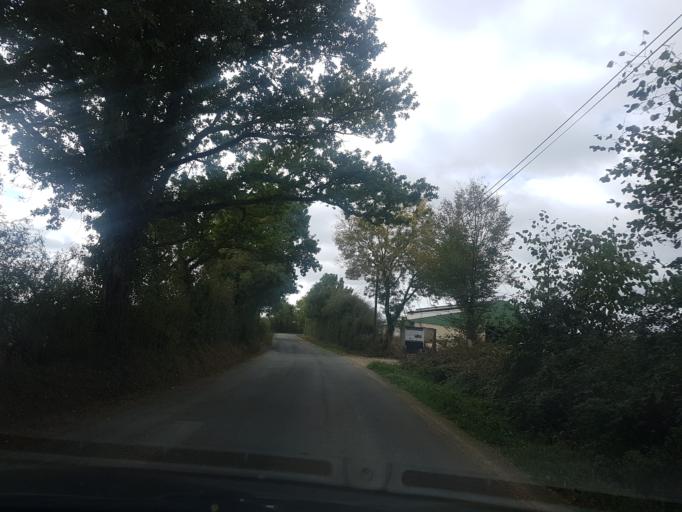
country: FR
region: Pays de la Loire
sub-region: Departement de la Loire-Atlantique
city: Ligne
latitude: 47.4032
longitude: -1.3925
